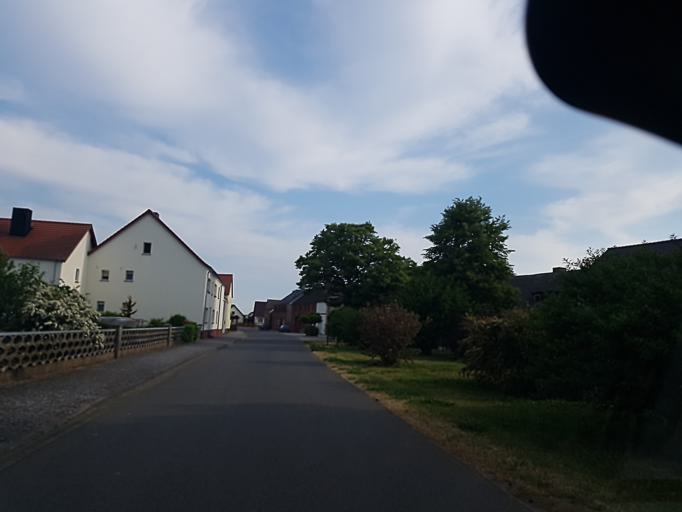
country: DE
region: Saxony-Anhalt
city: Seyda
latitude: 51.9041
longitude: 12.9101
